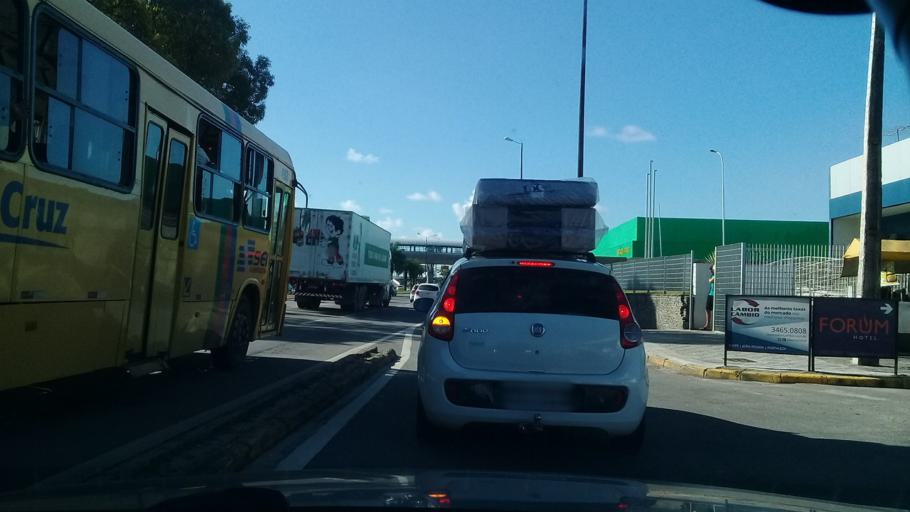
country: BR
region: Pernambuco
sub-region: Recife
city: Recife
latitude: -8.1343
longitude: -34.9165
